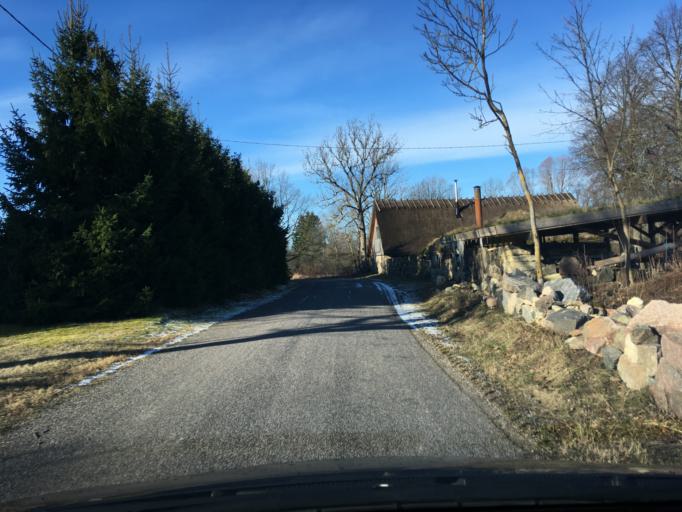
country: EE
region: Laeaene
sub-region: Lihula vald
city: Lihula
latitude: 58.5850
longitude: 23.7080
